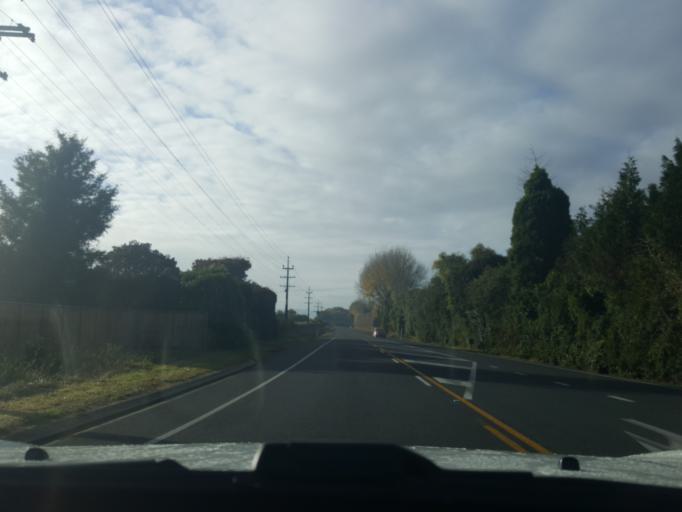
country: NZ
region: Waikato
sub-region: Hamilton City
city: Hamilton
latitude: -37.7753
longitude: 175.3742
